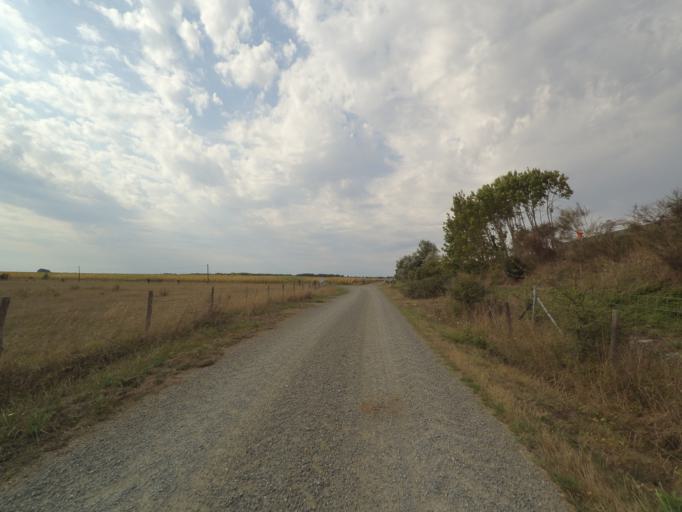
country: FR
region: Pays de la Loire
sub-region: Departement de la Vendee
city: Bouffere
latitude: 46.9836
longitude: -1.3785
